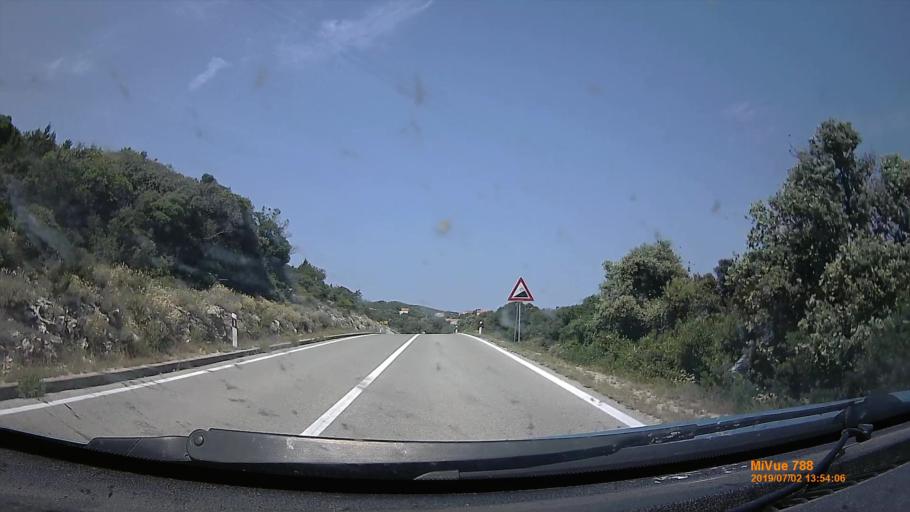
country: HR
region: Primorsko-Goranska
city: Mali Losinj
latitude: 44.6351
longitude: 14.3921
